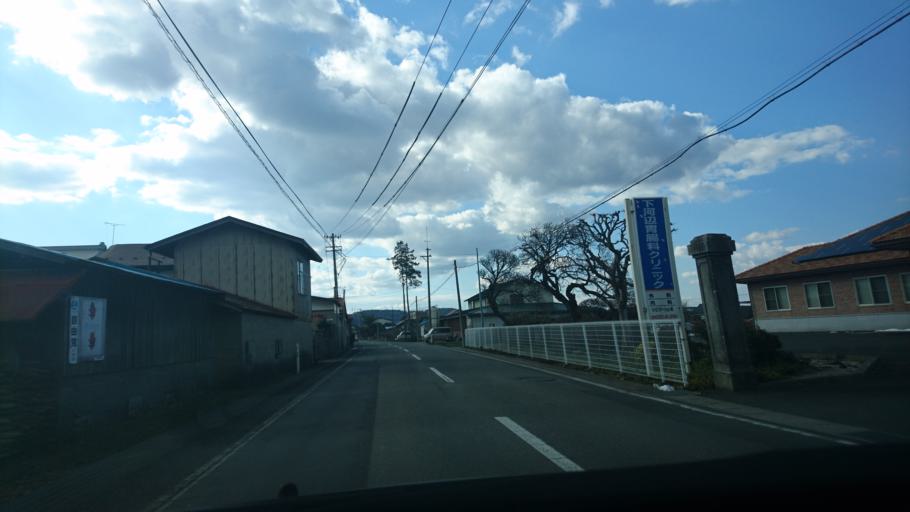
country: JP
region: Iwate
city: Mizusawa
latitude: 39.0432
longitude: 141.1398
